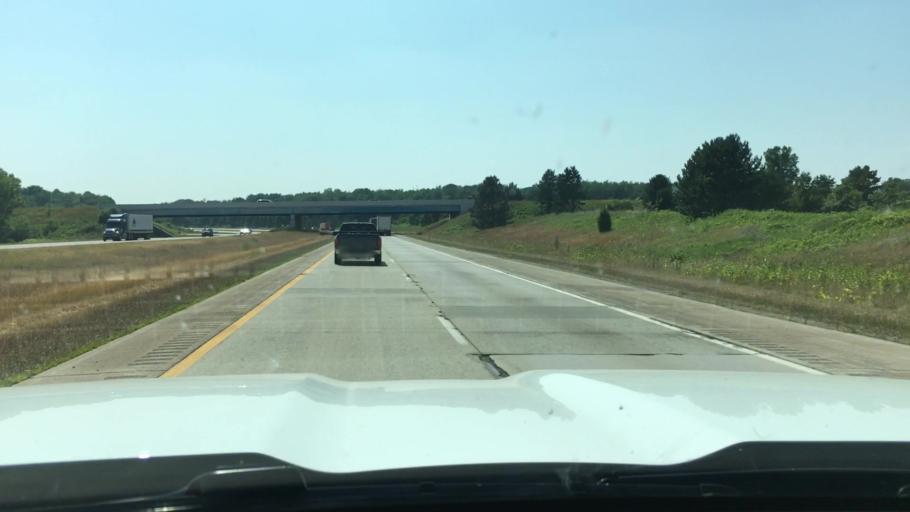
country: US
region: Michigan
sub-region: Clinton County
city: DeWitt
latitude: 42.8167
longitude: -84.5697
